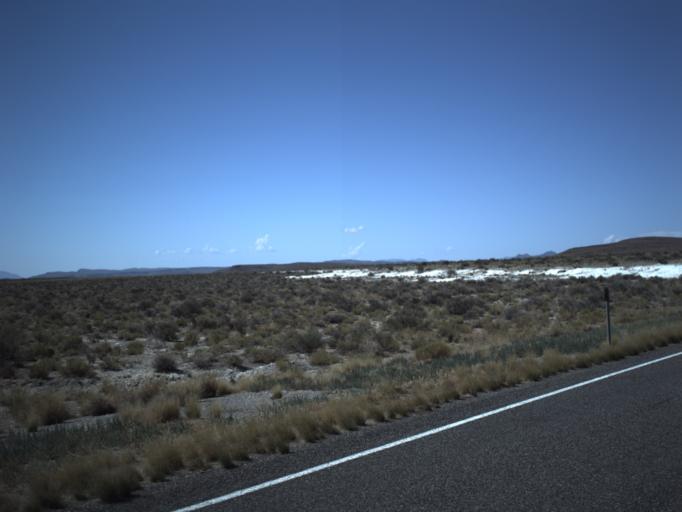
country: US
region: Utah
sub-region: Beaver County
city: Milford
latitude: 39.0610
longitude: -113.2447
